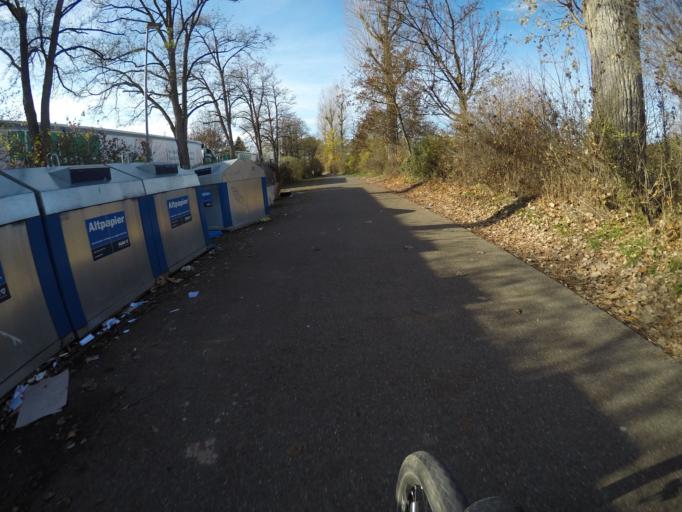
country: DE
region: Baden-Wuerttemberg
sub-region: Regierungsbezirk Stuttgart
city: Winterbach
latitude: 48.8070
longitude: 9.4365
